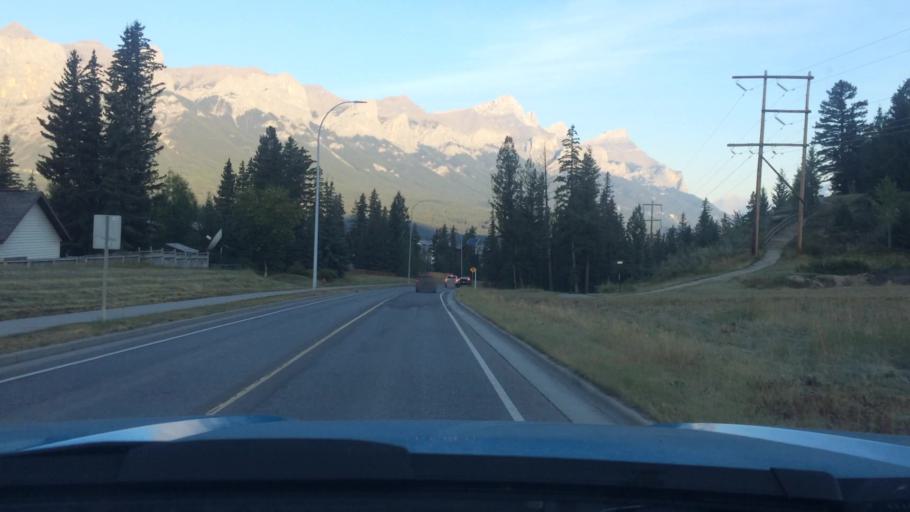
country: CA
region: Alberta
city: Canmore
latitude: 51.0875
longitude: -115.3329
